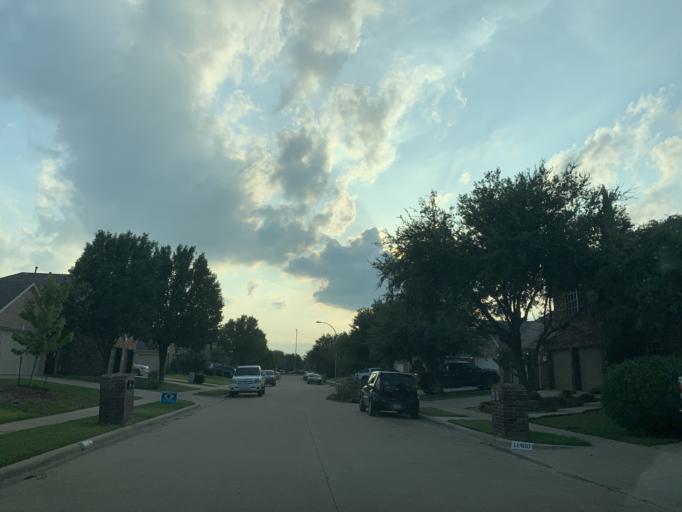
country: US
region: Texas
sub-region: Tarrant County
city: Keller
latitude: 32.9402
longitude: -97.2708
